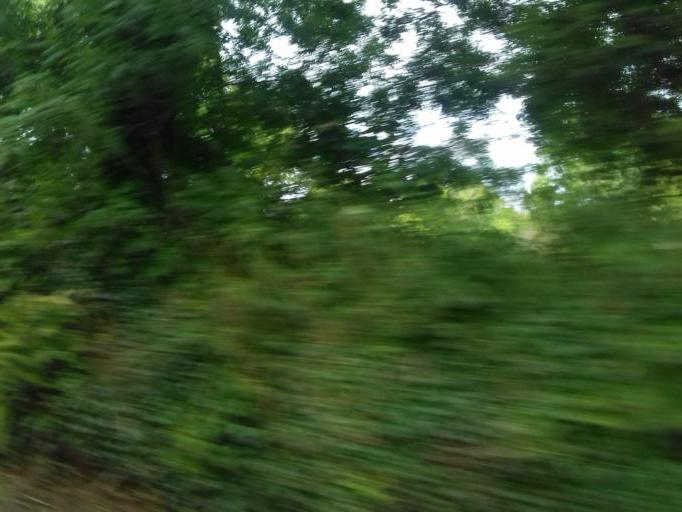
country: IE
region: Leinster
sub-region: Loch Garman
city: Loch Garman
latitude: 52.3147
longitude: -6.6487
